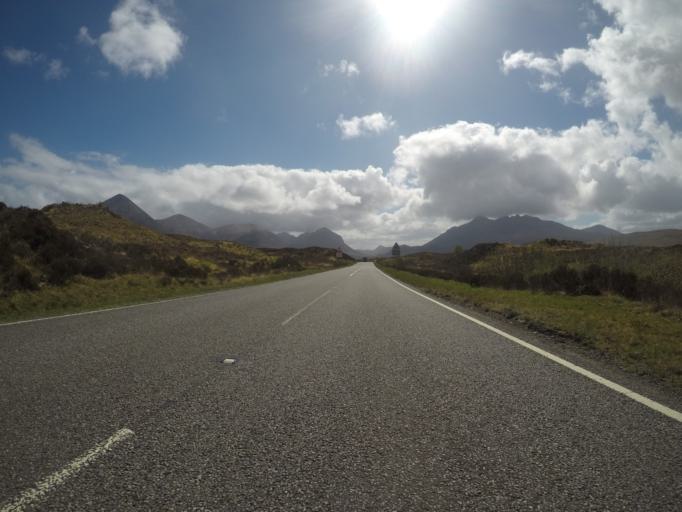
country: GB
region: Scotland
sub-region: Highland
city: Isle of Skye
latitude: 57.3077
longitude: -6.1891
